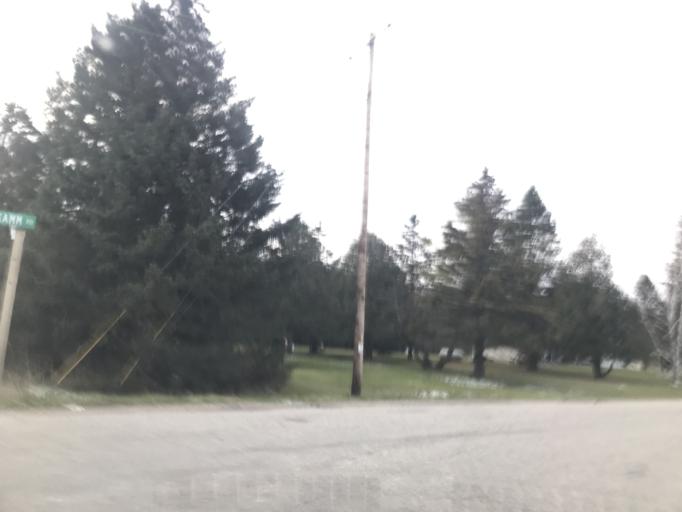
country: US
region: Wisconsin
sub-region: Marinette County
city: Peshtigo
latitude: 45.0584
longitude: -87.7936
